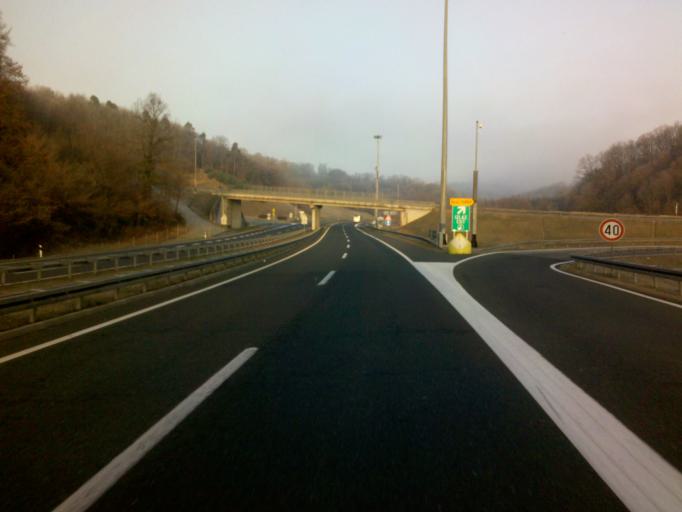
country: HR
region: Varazdinska
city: Ljubescica
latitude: 46.2087
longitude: 16.4092
